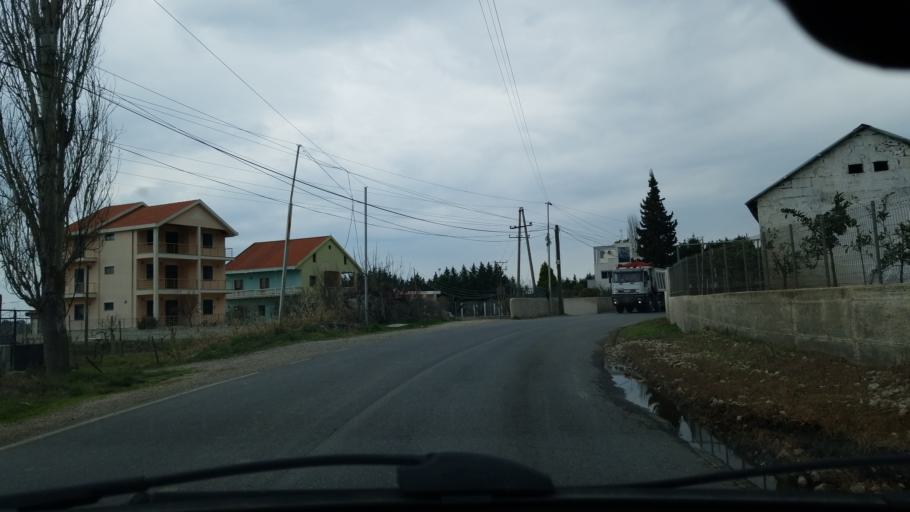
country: AL
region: Lezhe
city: Lezhe
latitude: 41.7902
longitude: 19.6247
